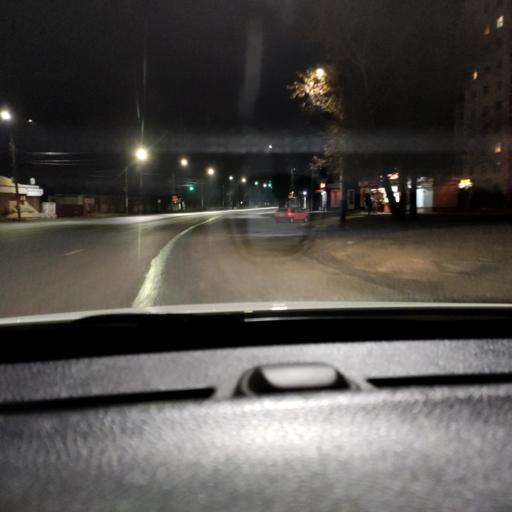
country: RU
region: Voronezj
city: Somovo
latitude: 51.7085
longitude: 39.2767
